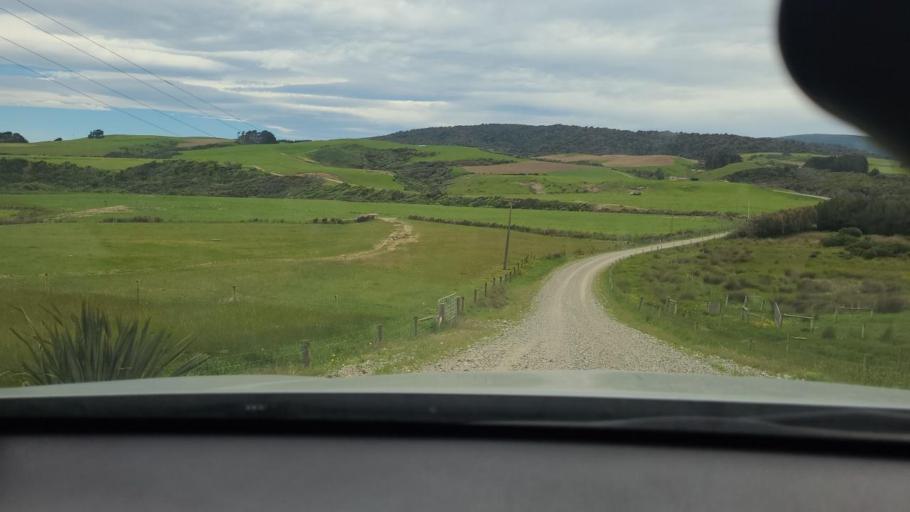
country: NZ
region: Southland
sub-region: Southland District
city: Riverton
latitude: -46.2613
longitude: 167.7366
